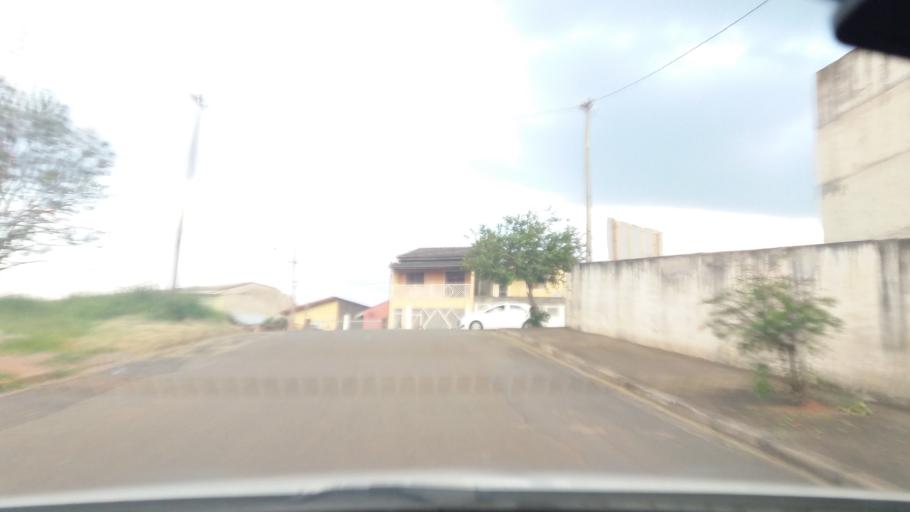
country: BR
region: Sao Paulo
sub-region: Bom Jesus Dos Perdoes
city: Bom Jesus dos Perdoes
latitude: -23.1441
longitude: -46.4651
